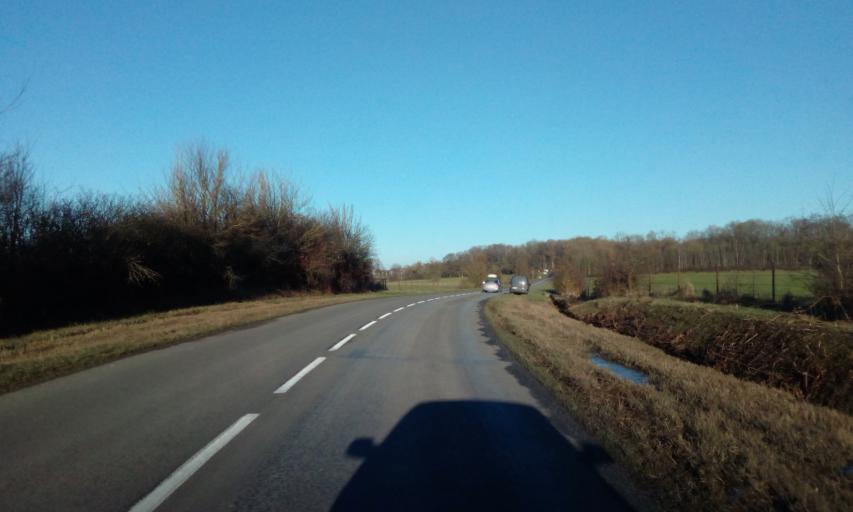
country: FR
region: Picardie
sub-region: Departement de l'Aisne
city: Rozoy-sur-Serre
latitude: 49.7363
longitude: 4.2886
